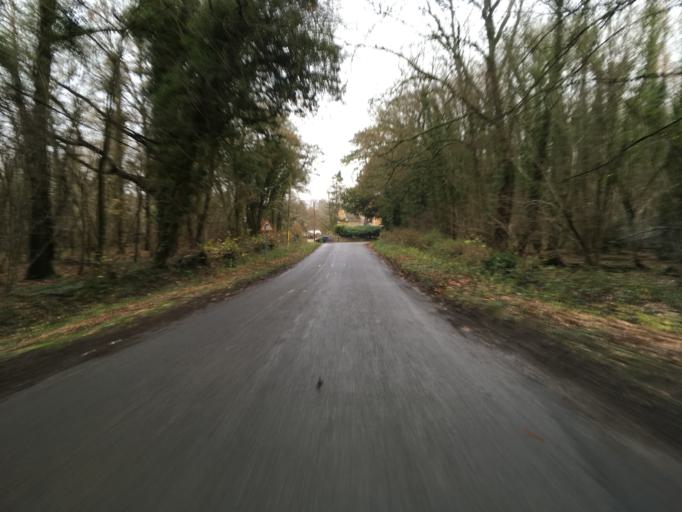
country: GB
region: England
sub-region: Wiltshire
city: Luckington
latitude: 51.5300
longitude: -2.2136
